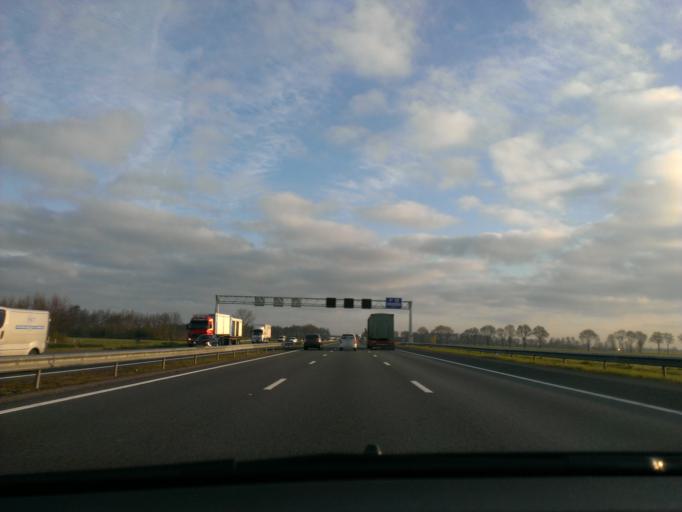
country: NL
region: Overijssel
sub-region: Gemeente Staphorst
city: Staphorst
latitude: 52.6124
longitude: 6.2074
